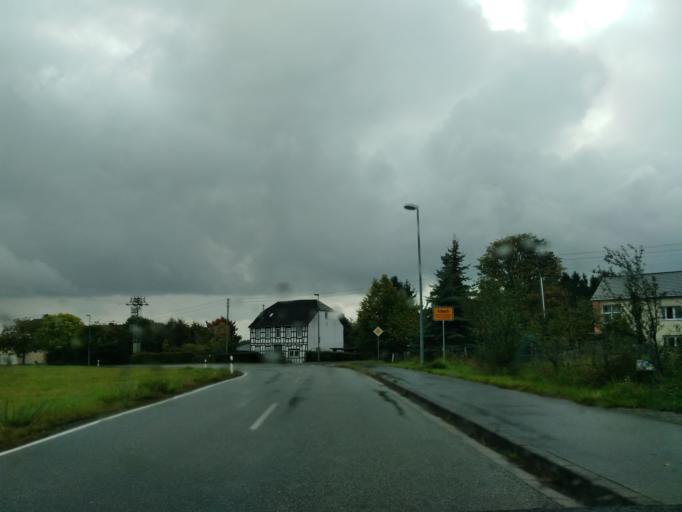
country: DE
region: Rheinland-Pfalz
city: Asbach
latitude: 50.6806
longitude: 7.4330
